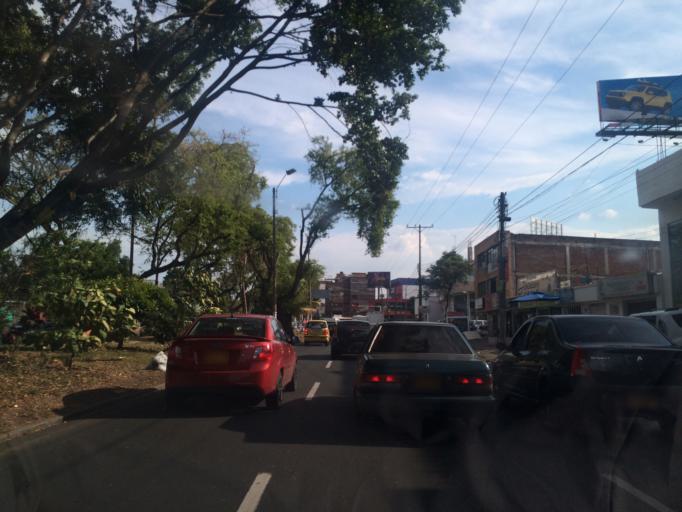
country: CO
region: Valle del Cauca
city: Cali
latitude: 3.3994
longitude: -76.5376
